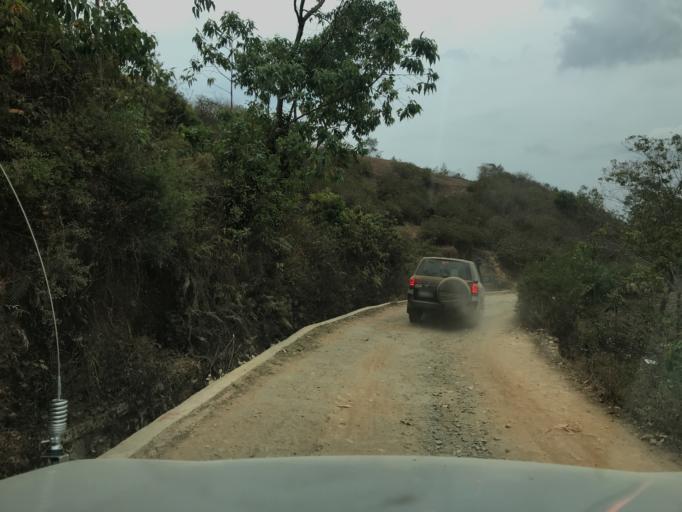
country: TL
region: Ermera
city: Gleno
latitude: -8.8379
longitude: 125.4364
